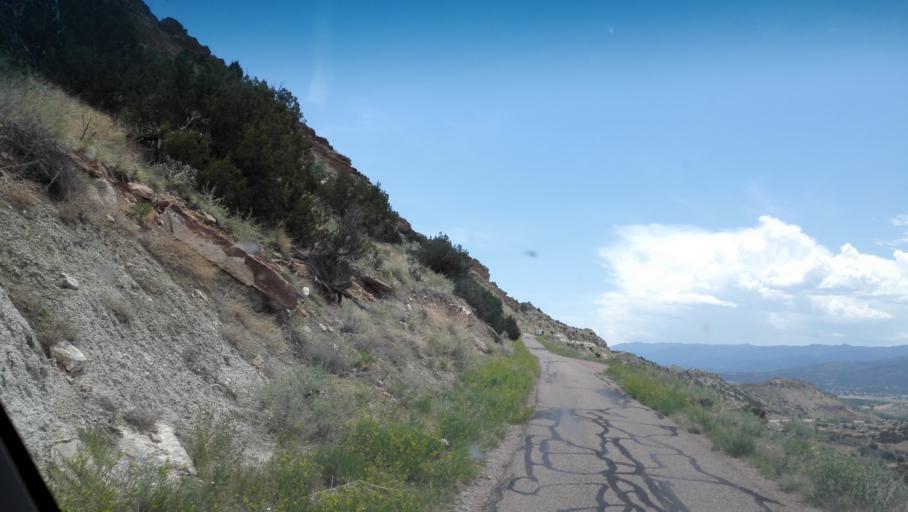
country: US
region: Colorado
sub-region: Fremont County
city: Canon City
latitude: 38.4695
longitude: -105.2553
